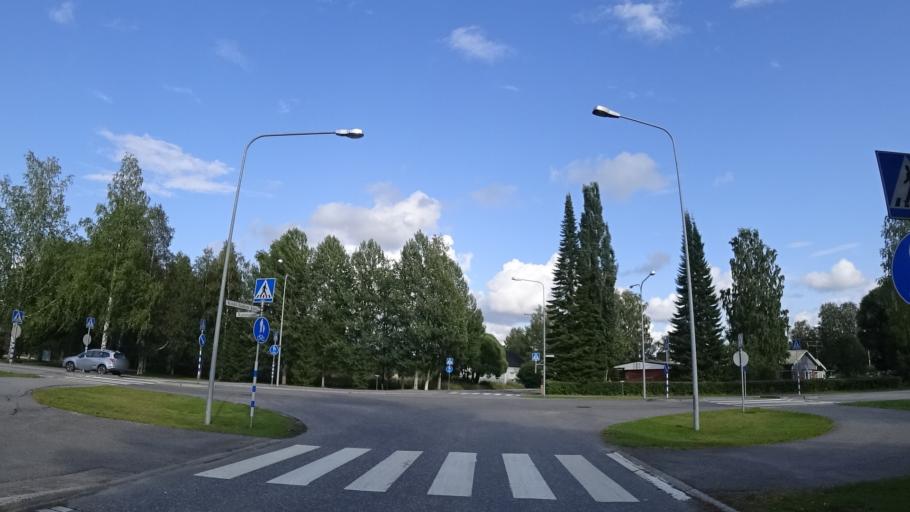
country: FI
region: North Karelia
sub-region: Pielisen Karjala
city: Lieksa
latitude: 63.3241
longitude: 30.0219
